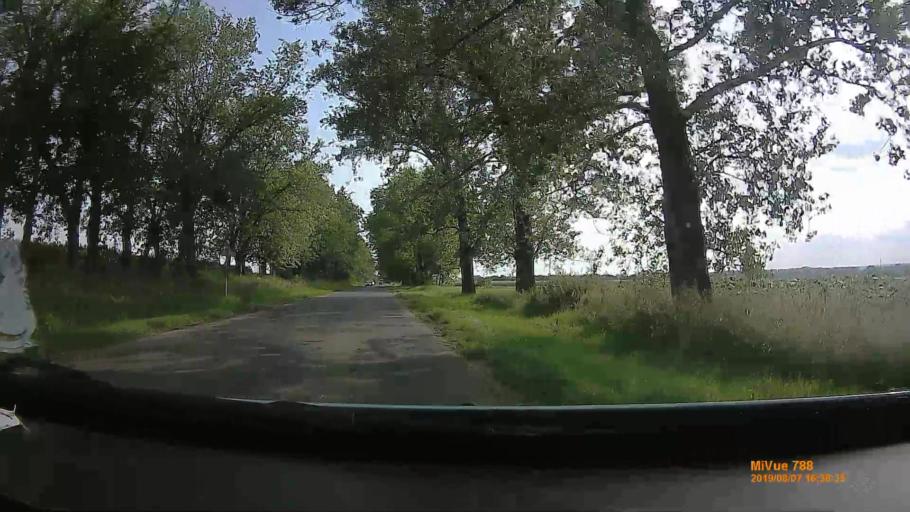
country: HU
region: Borsod-Abauj-Zemplen
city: Gonc
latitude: 48.4017
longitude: 21.2277
